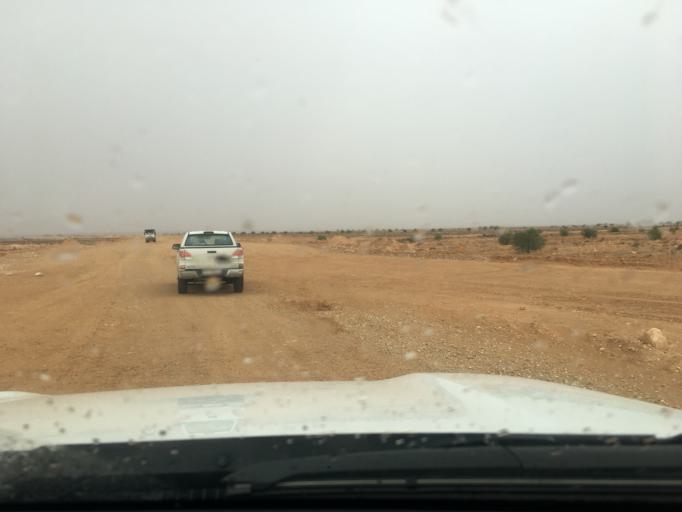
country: TN
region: Tataouine
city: Tataouine
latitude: 33.1311
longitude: 10.5017
